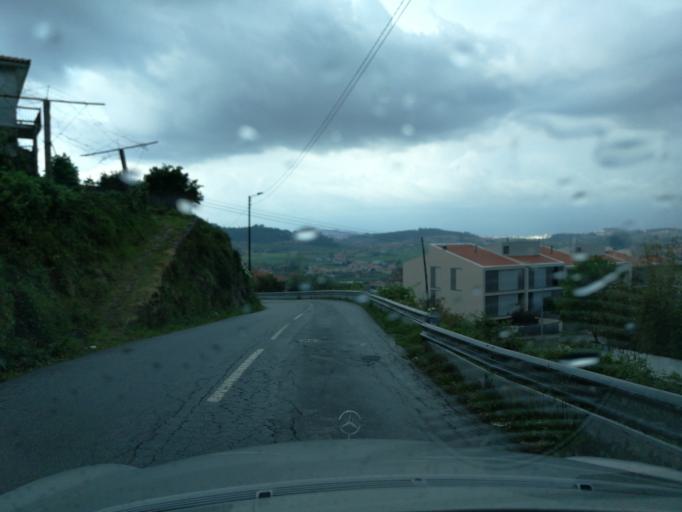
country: PT
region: Braga
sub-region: Vila Nova de Famalicao
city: Joane
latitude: 41.4799
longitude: -8.4252
